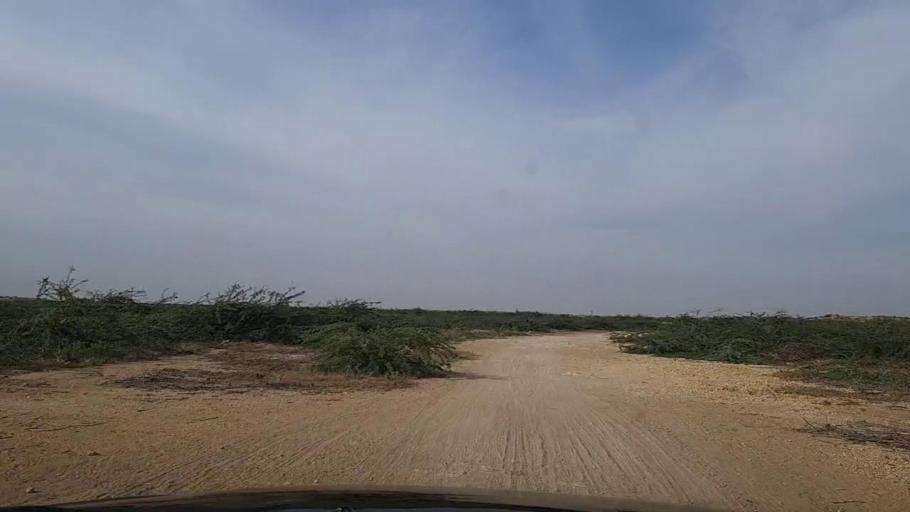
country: PK
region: Sindh
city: Gharo
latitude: 24.7827
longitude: 67.5601
